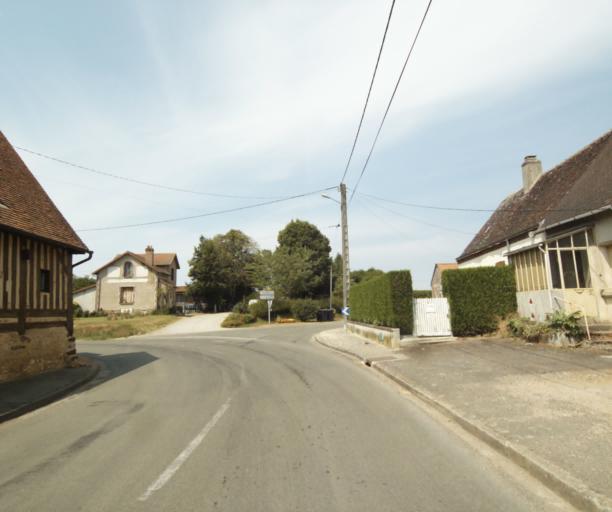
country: FR
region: Centre
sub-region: Departement d'Eure-et-Loir
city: La Bazoche-Gouet
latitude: 48.1740
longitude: 0.9951
